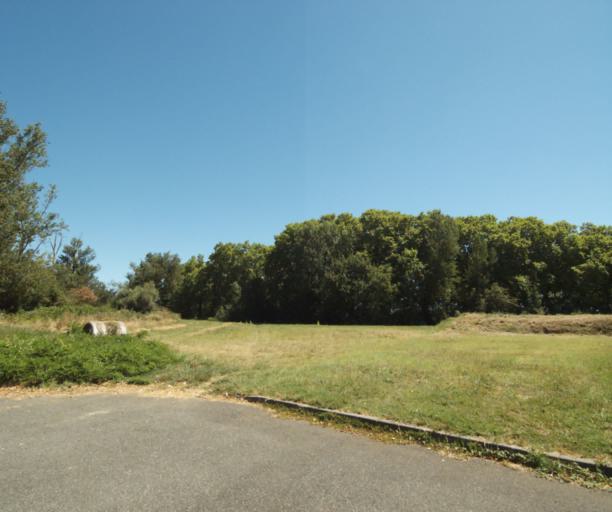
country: FR
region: Midi-Pyrenees
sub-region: Departement de la Haute-Garonne
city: Pechabou
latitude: 43.5144
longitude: 1.5149
